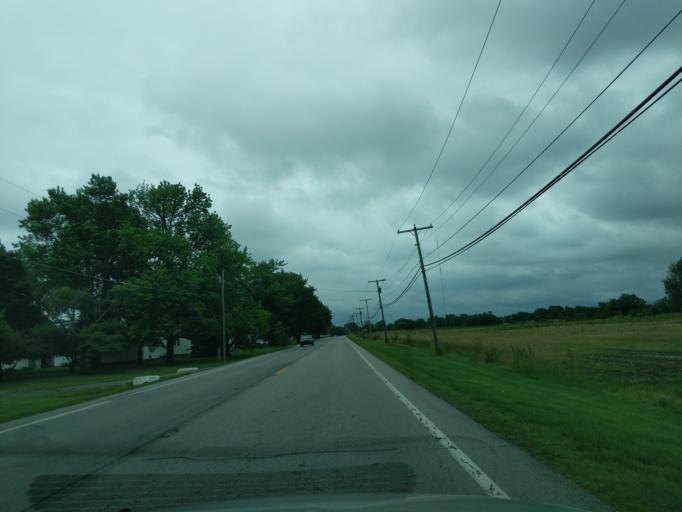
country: US
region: Indiana
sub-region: Madison County
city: Elwood
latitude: 40.2768
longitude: -85.8691
